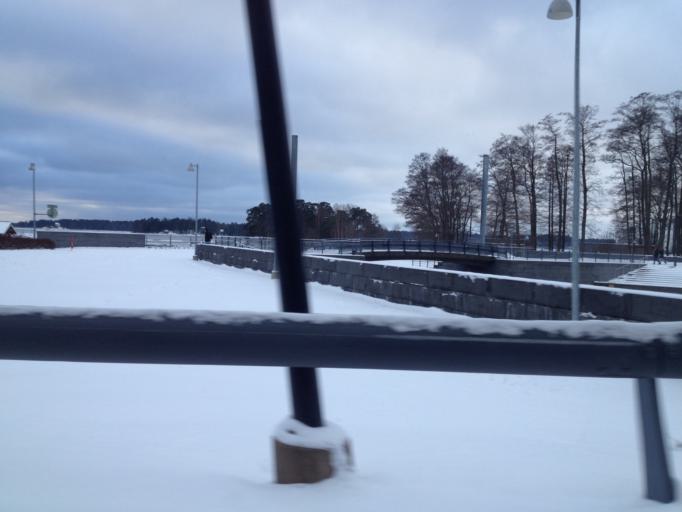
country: FI
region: Uusimaa
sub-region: Helsinki
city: Vantaa
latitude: 60.2029
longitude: 25.1624
